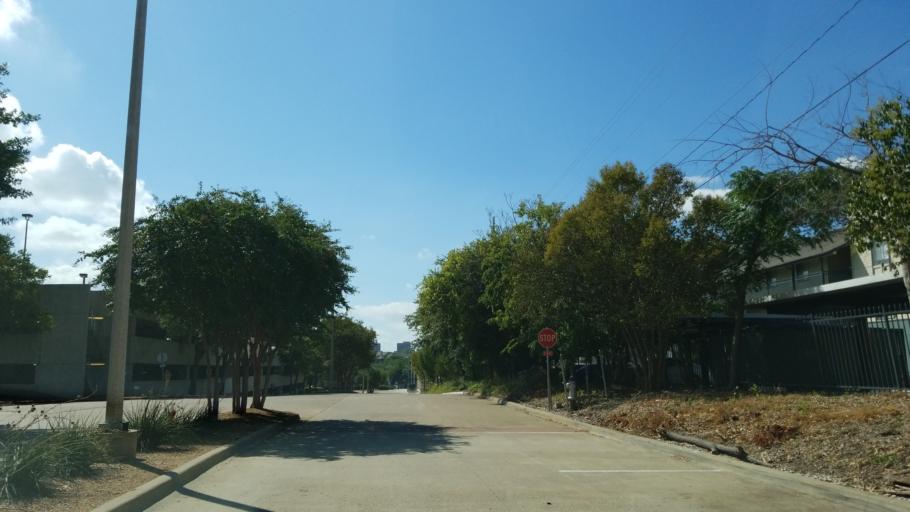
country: US
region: Texas
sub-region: Dallas County
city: Addison
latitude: 32.9502
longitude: -96.8065
